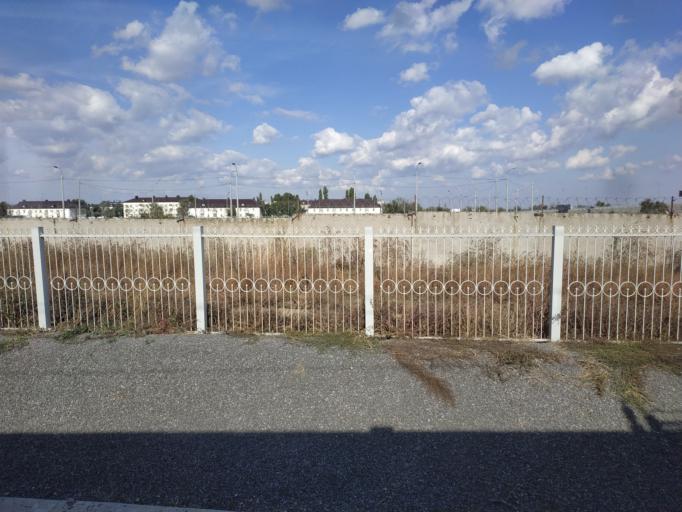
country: RU
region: Volgograd
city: Gumrak
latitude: 48.7934
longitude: 44.3604
